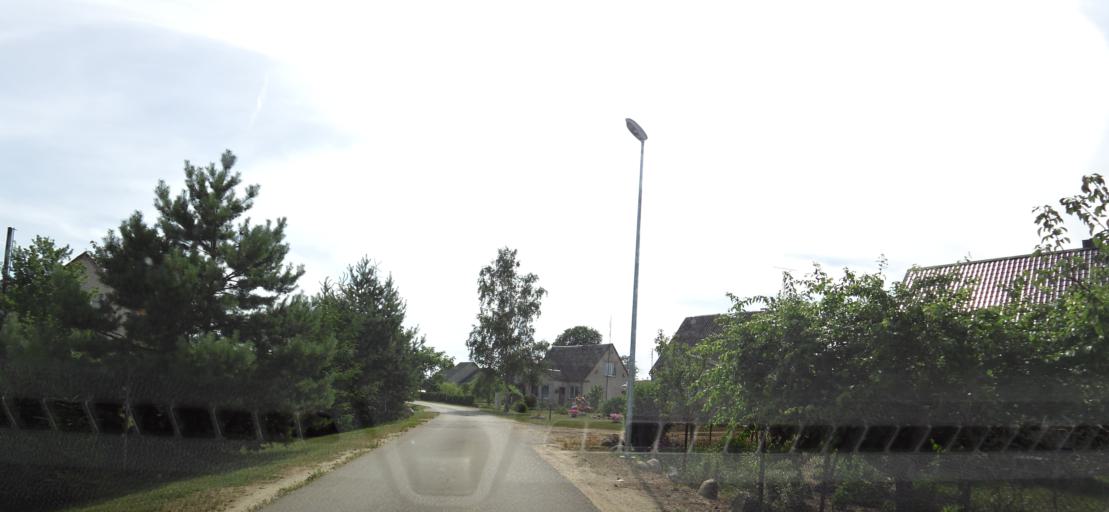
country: LT
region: Panevezys
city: Pasvalys
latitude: 55.9337
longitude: 24.3497
